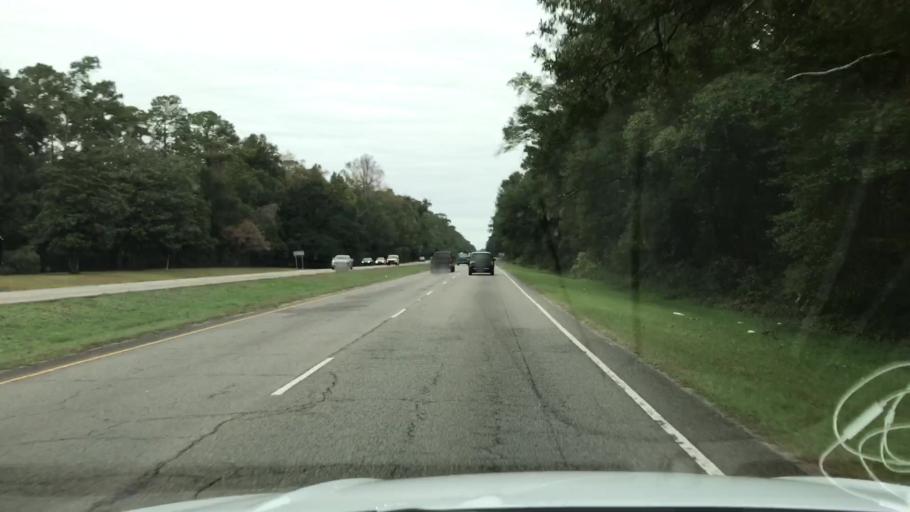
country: US
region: South Carolina
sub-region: Georgetown County
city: Murrells Inlet
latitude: 33.5104
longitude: -79.0756
